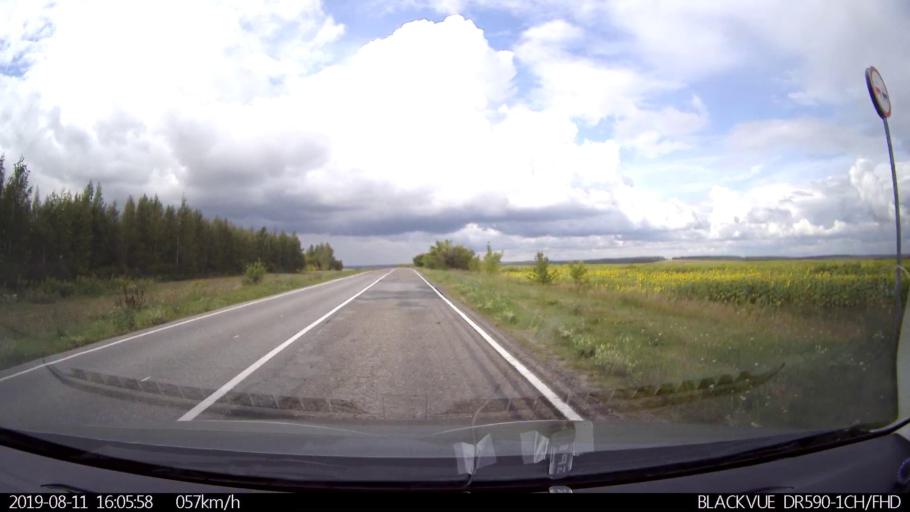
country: RU
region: Ulyanovsk
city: Ignatovka
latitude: 53.9649
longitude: 47.6492
